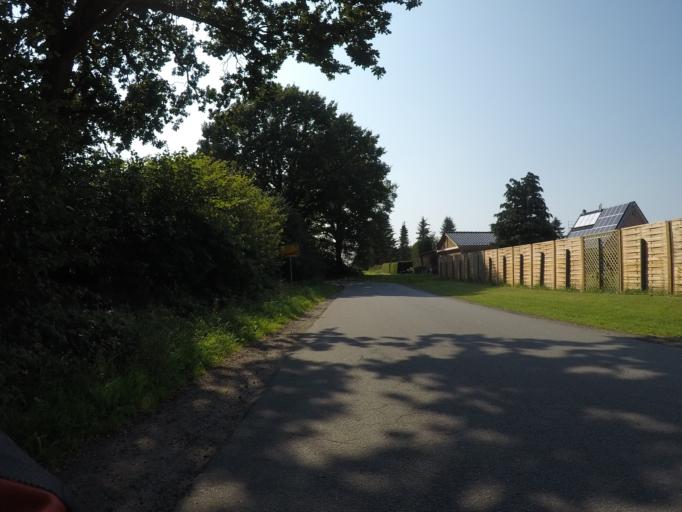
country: DE
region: Schleswig-Holstein
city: Todesfelde
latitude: 53.8889
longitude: 10.1754
